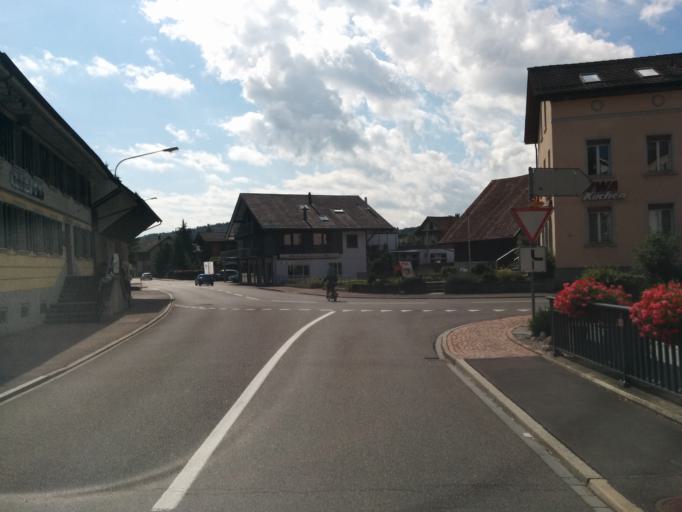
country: CH
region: Aargau
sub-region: Bezirk Bremgarten
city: Villmergen
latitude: 47.3452
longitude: 8.2453
